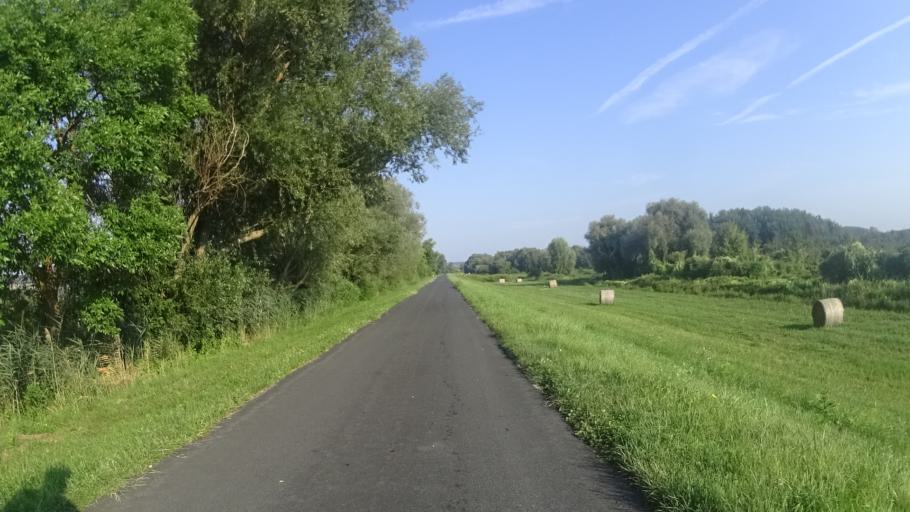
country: HU
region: Zala
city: Sarmellek
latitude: 46.6548
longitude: 17.1414
